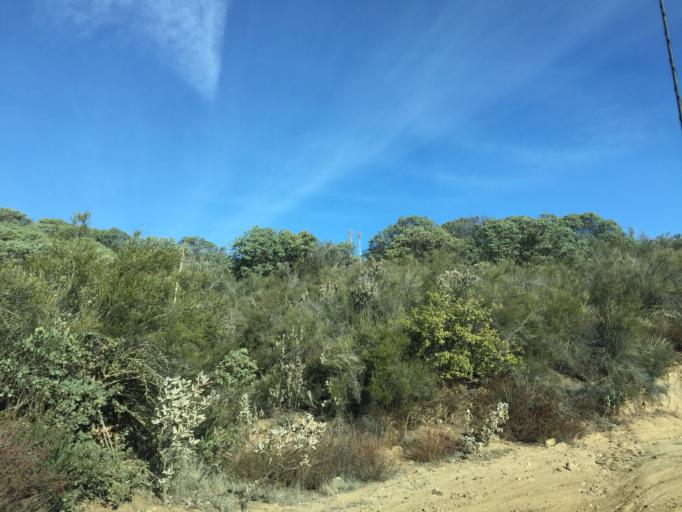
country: US
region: California
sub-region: Riverside County
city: Valle Vista
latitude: 33.6318
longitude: -116.8323
